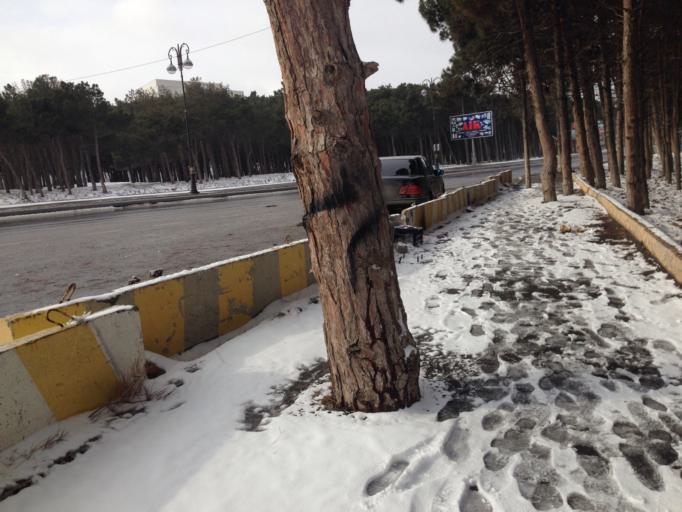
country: AZ
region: Baki
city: Baku
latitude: 40.3954
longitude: 49.8527
